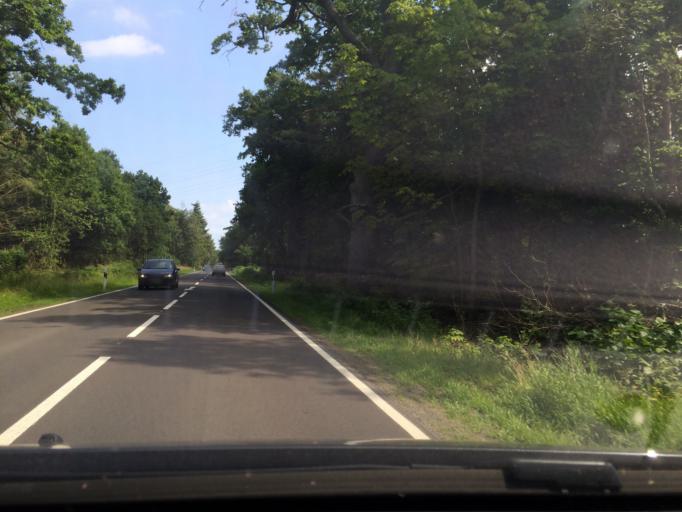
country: DE
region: Mecklenburg-Vorpommern
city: Ostseebad Binz
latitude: 54.4362
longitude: 13.5598
